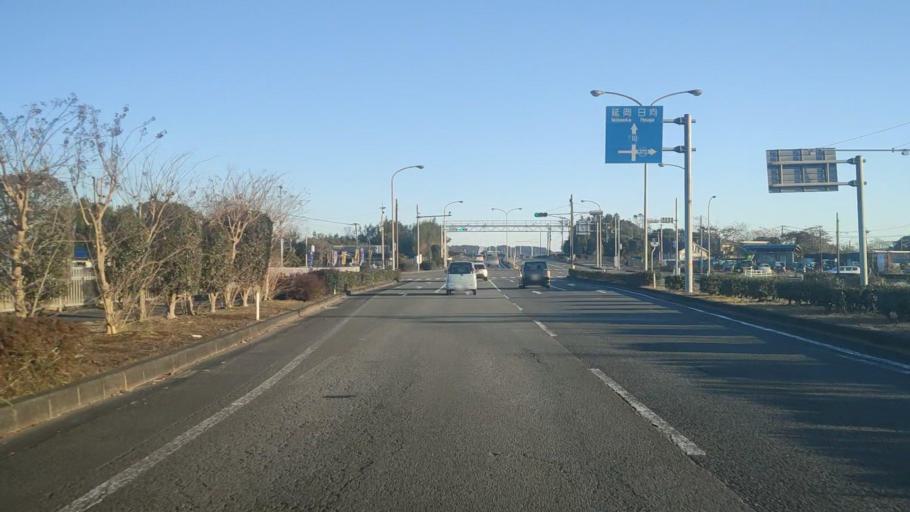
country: JP
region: Miyazaki
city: Tsuma
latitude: 32.0437
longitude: 131.4703
